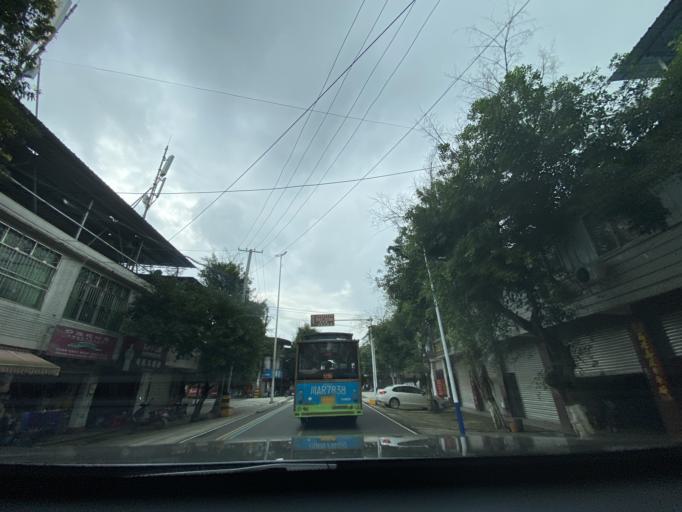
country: CN
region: Sichuan
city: Wujin
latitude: 30.4077
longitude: 103.9901
